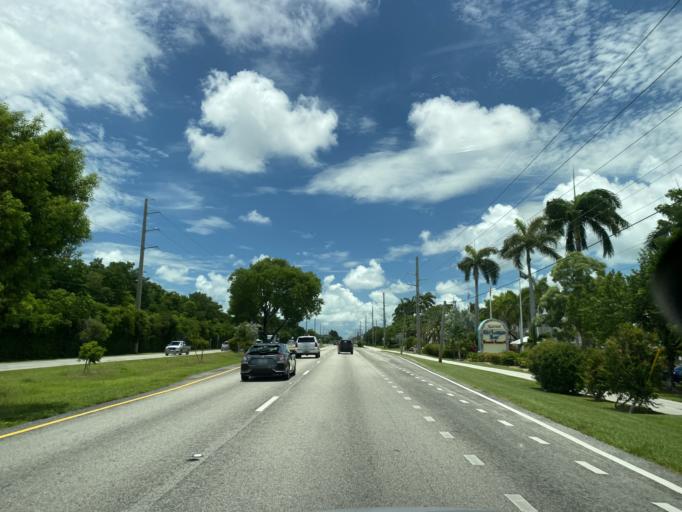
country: US
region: Florida
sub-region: Monroe County
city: Key Largo
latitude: 25.1420
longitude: -80.3989
